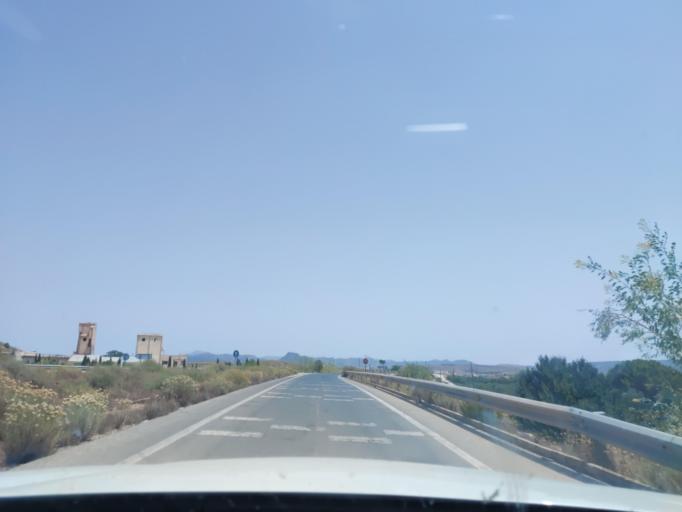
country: ES
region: Castille-La Mancha
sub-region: Provincia de Albacete
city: Hellin
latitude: 38.5012
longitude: -1.6739
